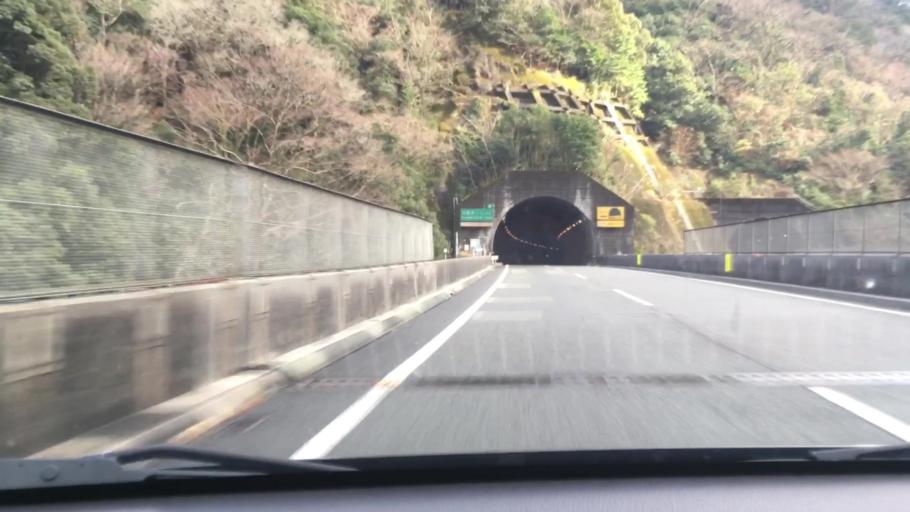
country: JP
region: Kumamoto
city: Hitoyoshi
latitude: 32.3376
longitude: 130.7334
